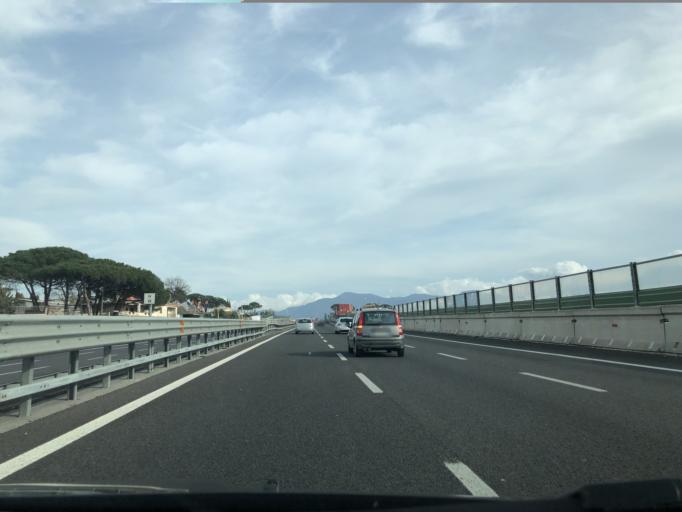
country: IT
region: Campania
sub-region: Provincia di Napoli
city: Torre del Greco
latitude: 40.7743
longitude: 14.4080
